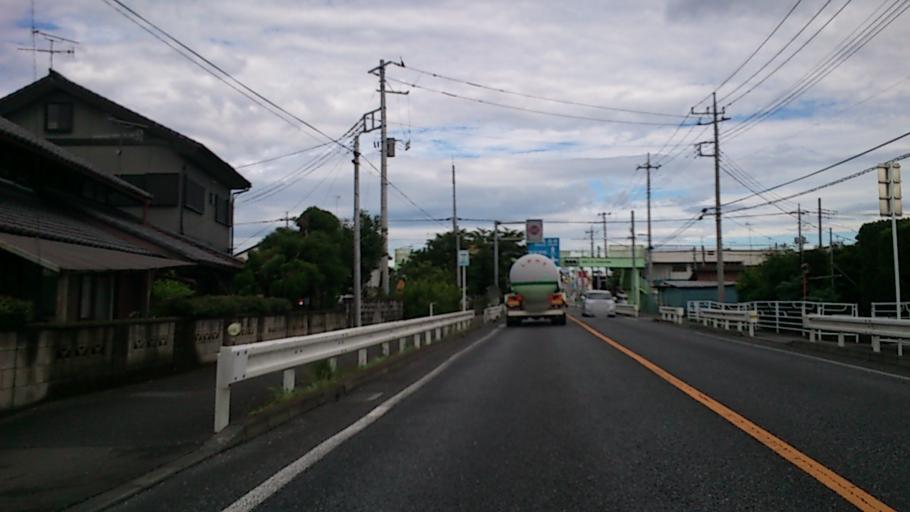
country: JP
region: Saitama
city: Honjo
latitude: 36.2580
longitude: 139.1530
